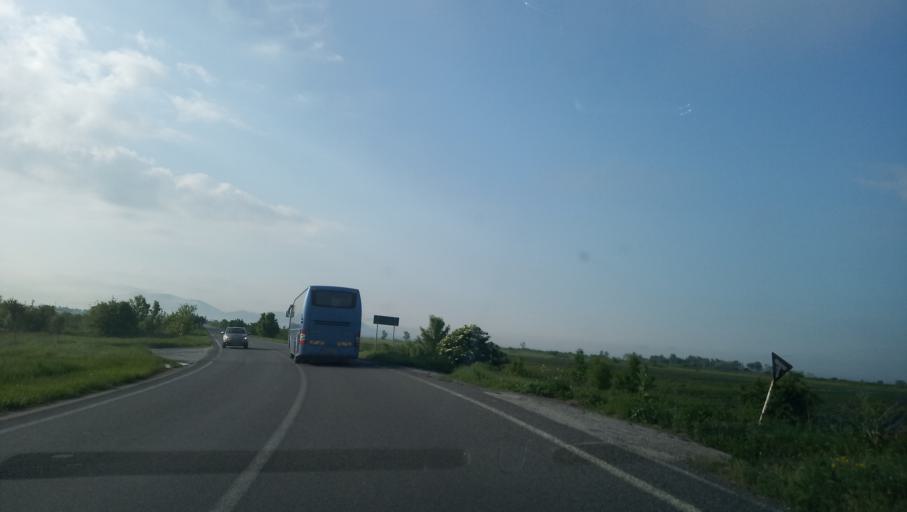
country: RO
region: Timis
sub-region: Comuna Moravita
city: Moravita
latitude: 45.2437
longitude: 21.2625
